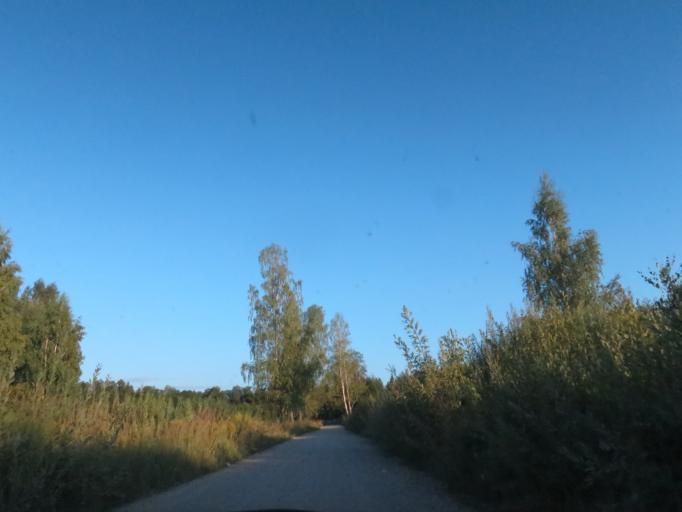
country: LV
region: Sigulda
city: Sigulda
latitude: 57.1658
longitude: 24.8224
